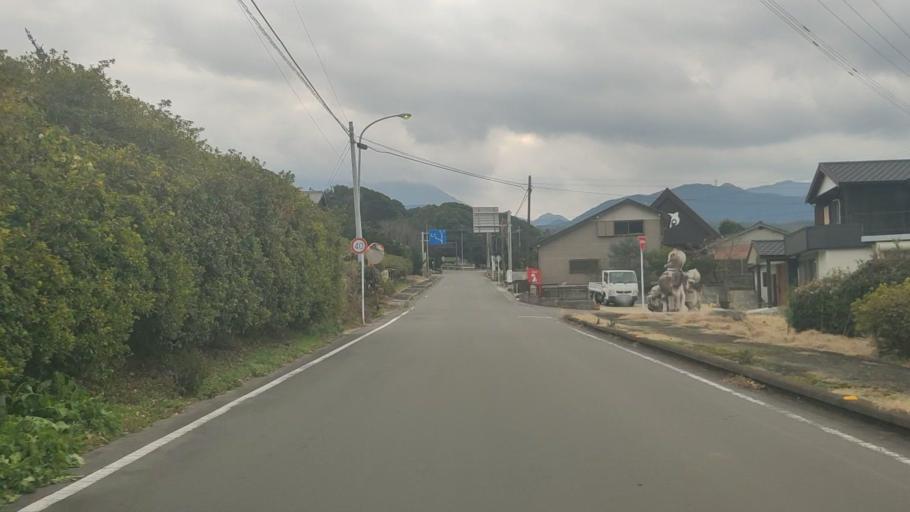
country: JP
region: Nagasaki
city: Shimabara
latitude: 32.8262
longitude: 130.2918
